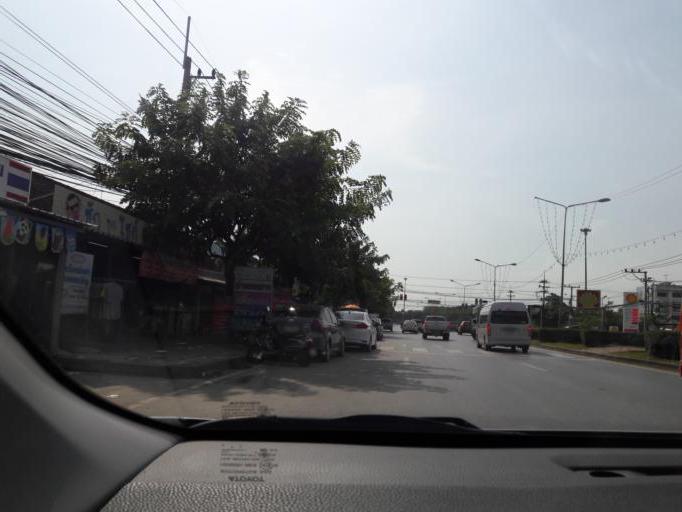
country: TH
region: Ang Thong
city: Ang Thong
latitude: 14.5866
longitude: 100.4552
